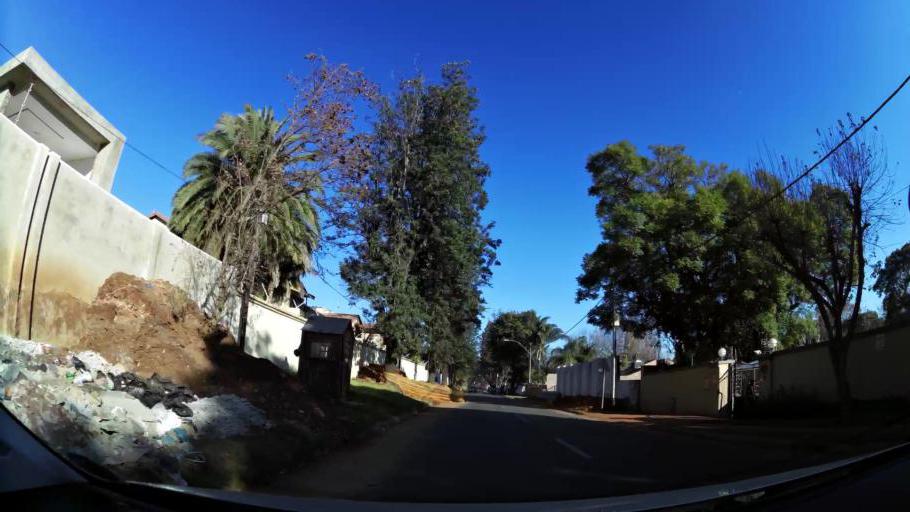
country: ZA
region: Gauteng
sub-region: City of Johannesburg Metropolitan Municipality
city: Johannesburg
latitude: -26.1691
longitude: 28.0705
